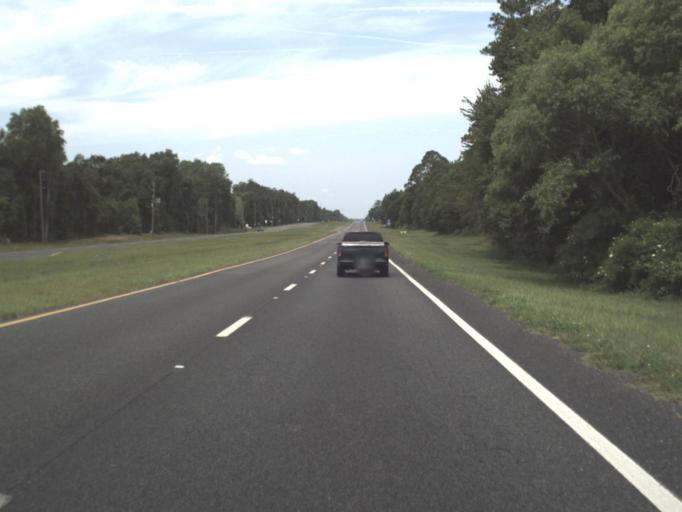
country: US
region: Florida
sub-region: Alachua County
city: Hawthorne
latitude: 29.5984
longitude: -82.1842
